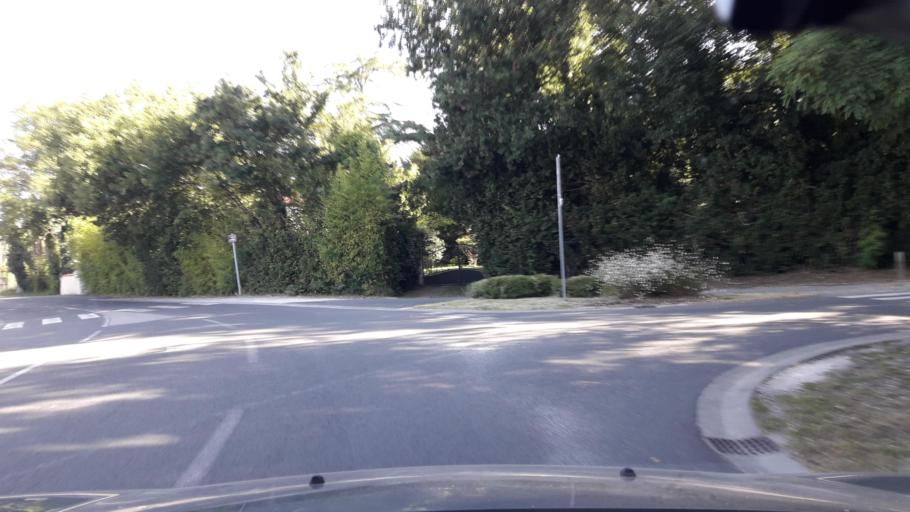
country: FR
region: Poitou-Charentes
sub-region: Departement de la Charente-Maritime
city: Etaules
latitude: 45.7286
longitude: -1.0994
